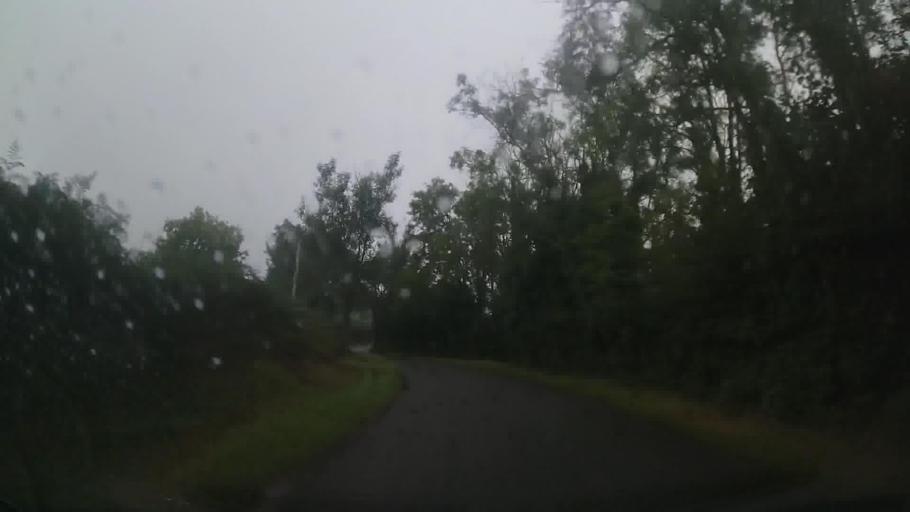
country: GB
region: Wales
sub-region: Carmarthenshire
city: Whitland
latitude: 51.7605
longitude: -4.6358
